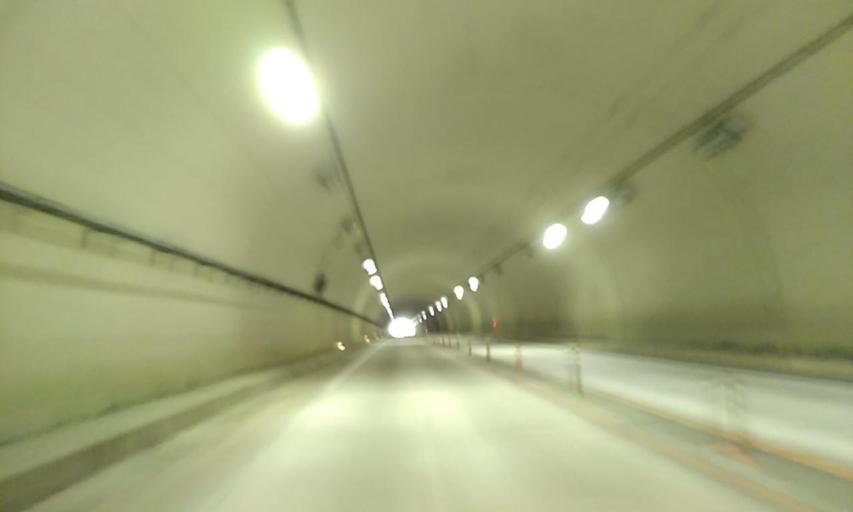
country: JP
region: Wakayama
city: Shingu
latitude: 33.6359
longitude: 135.9253
